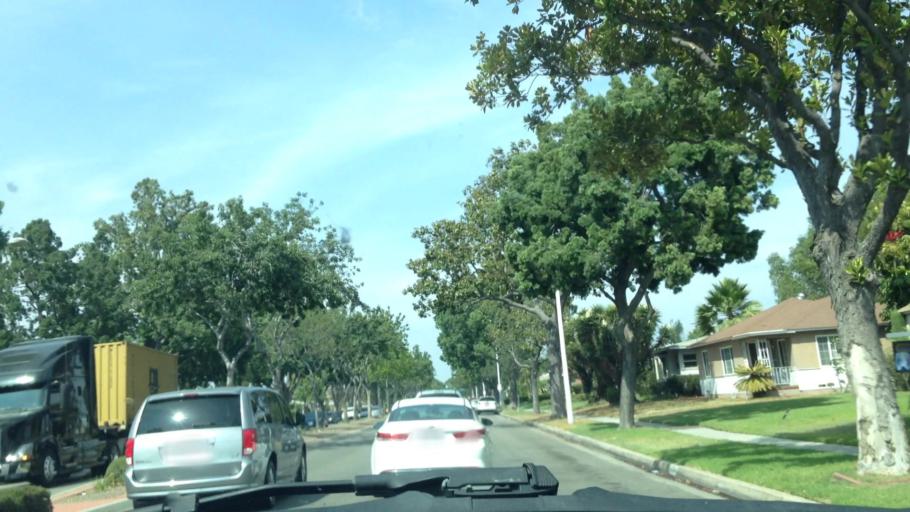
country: US
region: California
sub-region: Los Angeles County
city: Downey
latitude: 33.9570
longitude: -118.1274
